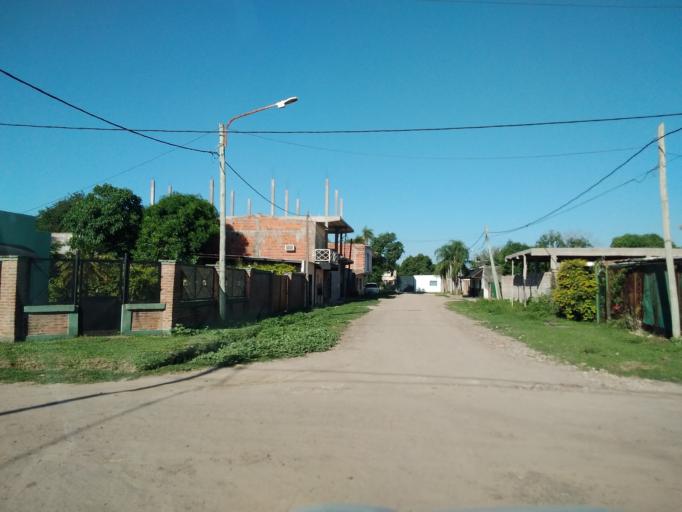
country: AR
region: Corrientes
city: Corrientes
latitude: -27.4861
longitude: -58.8119
